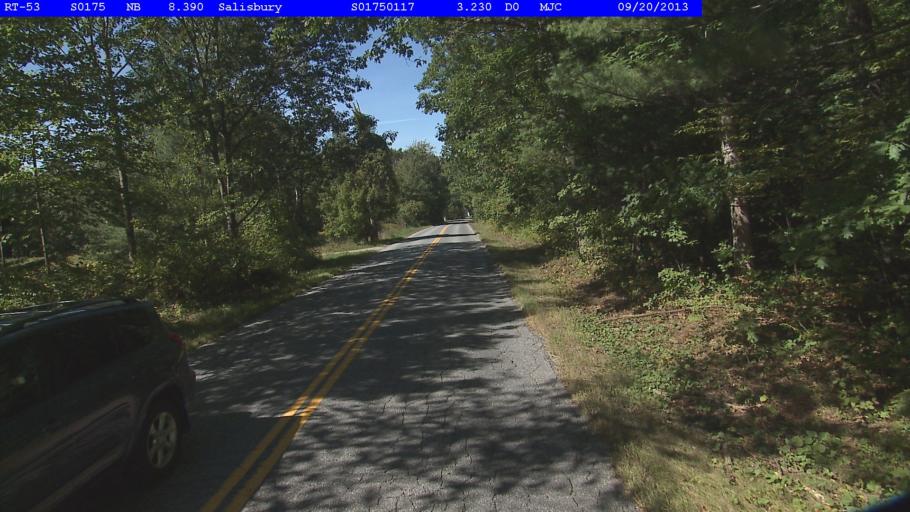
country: US
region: Vermont
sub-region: Addison County
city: Middlebury (village)
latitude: 43.9236
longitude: -73.0939
